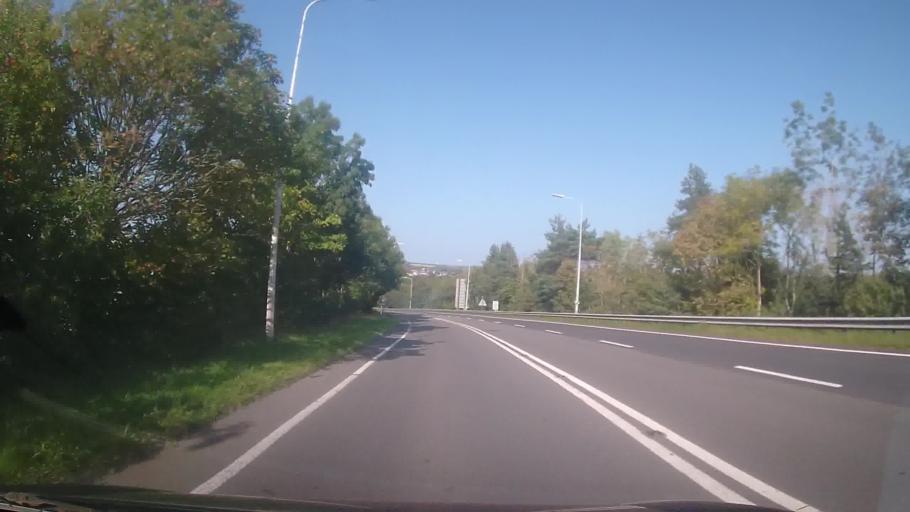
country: GB
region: Wales
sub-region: County of Ceredigion
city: Cardigan
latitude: 52.0776
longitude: -4.6548
